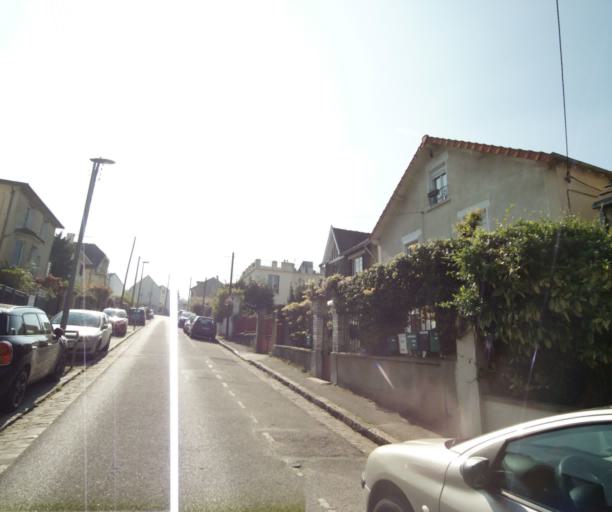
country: FR
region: Ile-de-France
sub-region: Departement des Hauts-de-Seine
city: Ville-d'Avray
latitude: 48.8186
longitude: 2.2039
